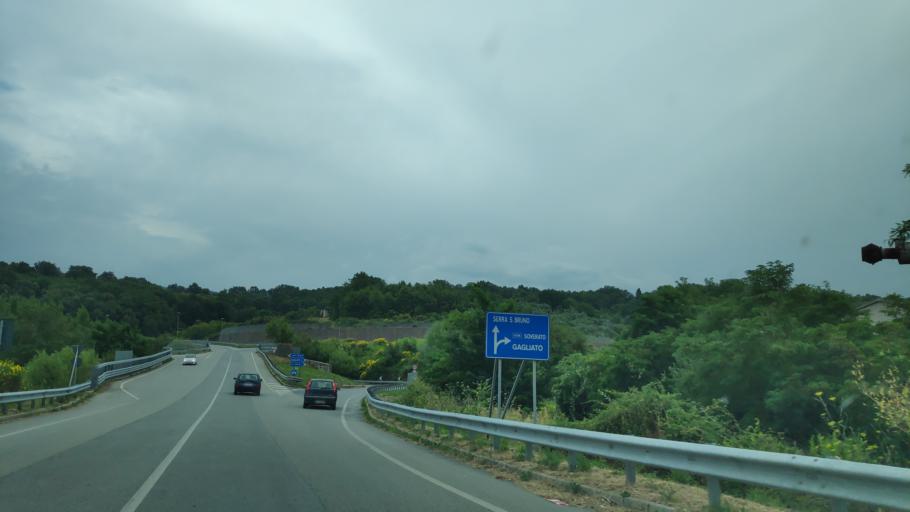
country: IT
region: Calabria
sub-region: Provincia di Catanzaro
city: Argusto
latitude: 38.6820
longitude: 16.4247
